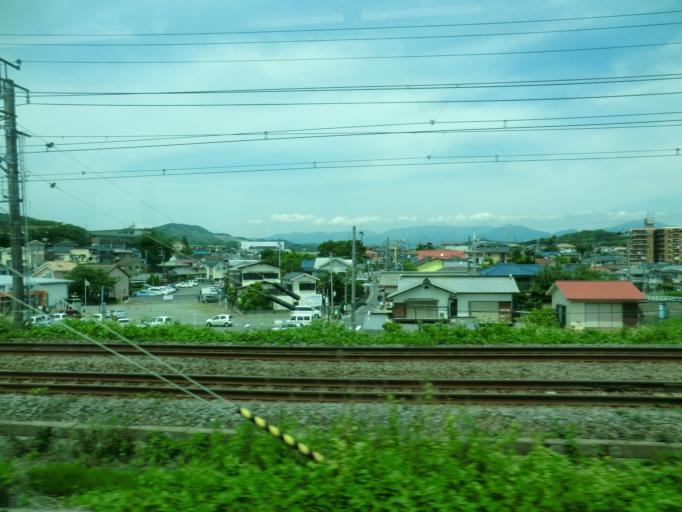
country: JP
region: Kanagawa
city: Ninomiya
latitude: 35.2914
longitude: 139.2352
